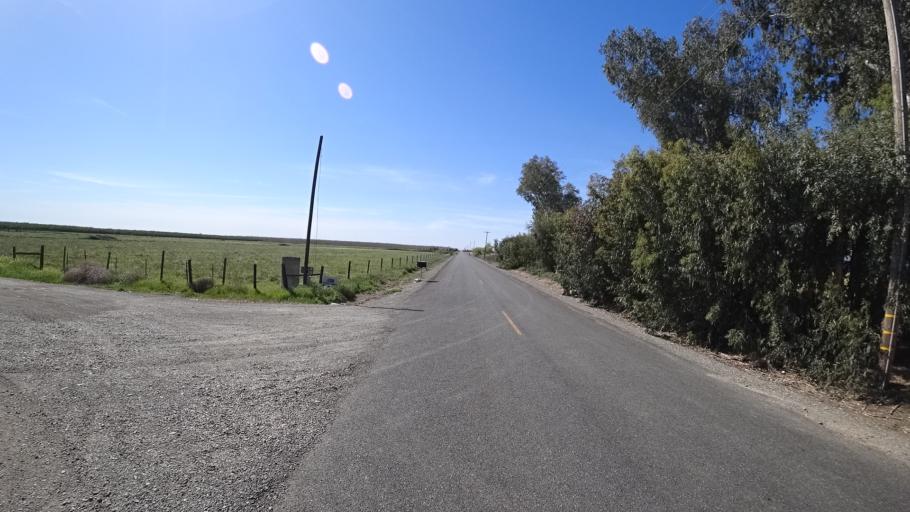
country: US
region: California
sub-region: Glenn County
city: Hamilton City
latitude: 39.6597
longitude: -122.1035
